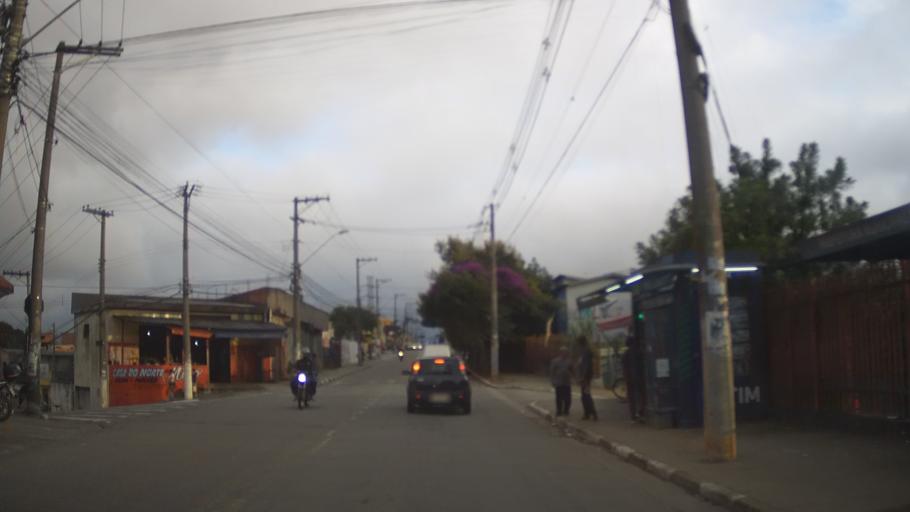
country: BR
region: Sao Paulo
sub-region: Itaquaquecetuba
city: Itaquaquecetuba
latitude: -23.4562
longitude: -46.4236
